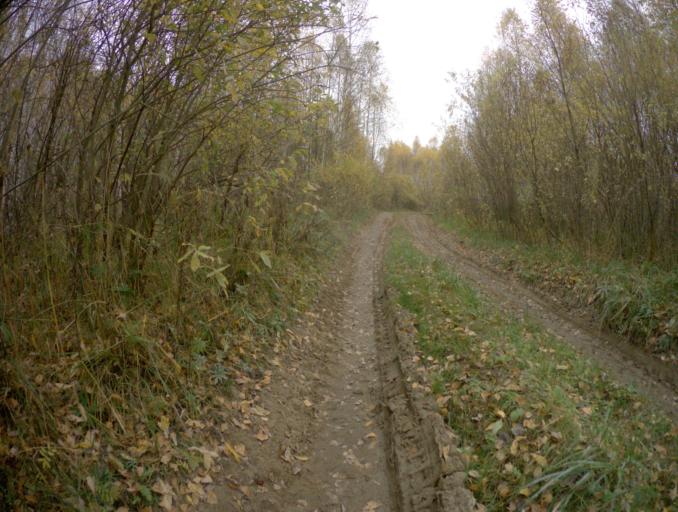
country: RU
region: Vladimir
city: Golovino
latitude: 55.9381
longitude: 40.3775
